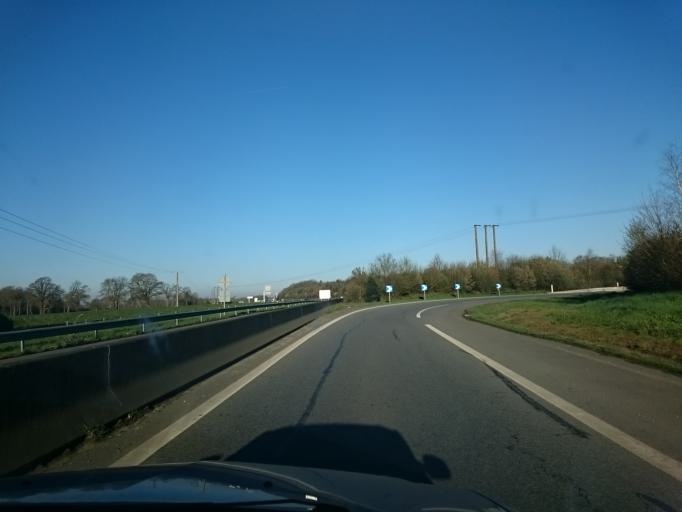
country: FR
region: Brittany
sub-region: Departement d'Ille-et-Vilaine
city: Chantepie
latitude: 48.0820
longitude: -1.6428
